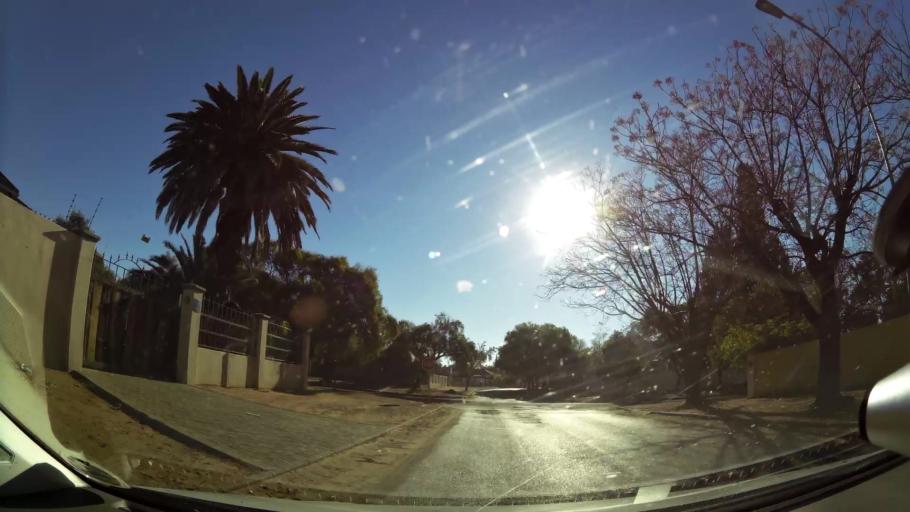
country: ZA
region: Northern Cape
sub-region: Frances Baard District Municipality
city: Kimberley
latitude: -28.7542
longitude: 24.7788
